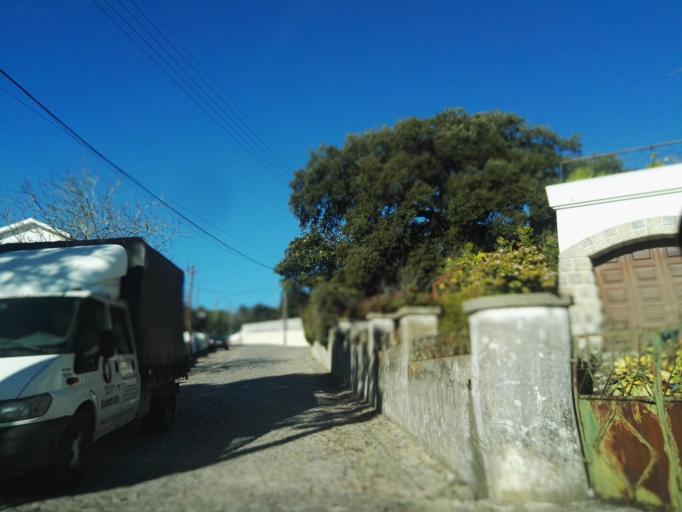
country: PT
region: Lisbon
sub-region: Mafra
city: Venda do Pinheiro
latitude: 38.9282
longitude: -9.2365
